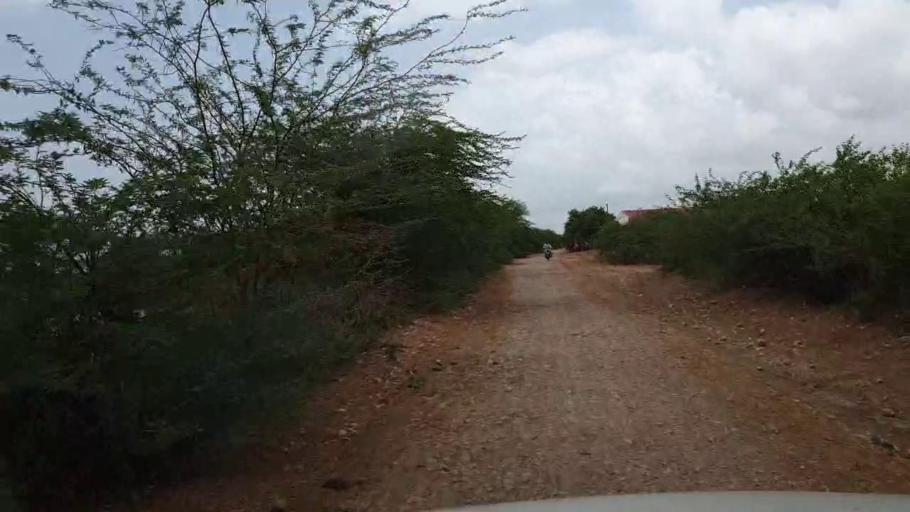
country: PK
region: Sindh
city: Kario
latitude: 24.6904
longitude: 68.6654
